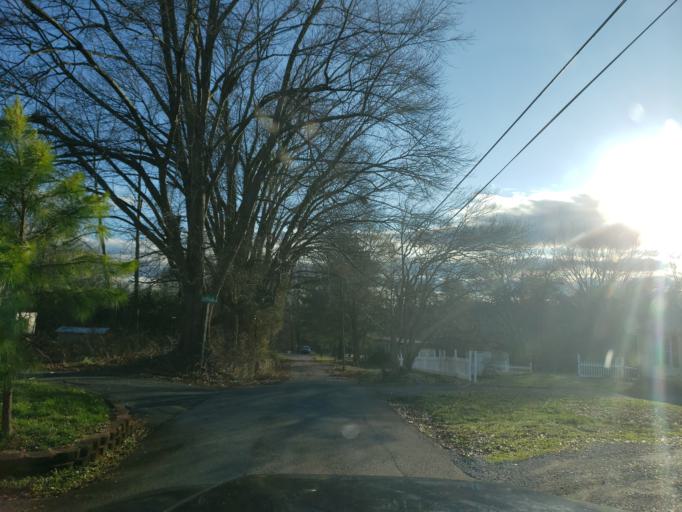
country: US
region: North Carolina
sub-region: Cleveland County
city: Shelby
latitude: 35.4162
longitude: -81.5591
